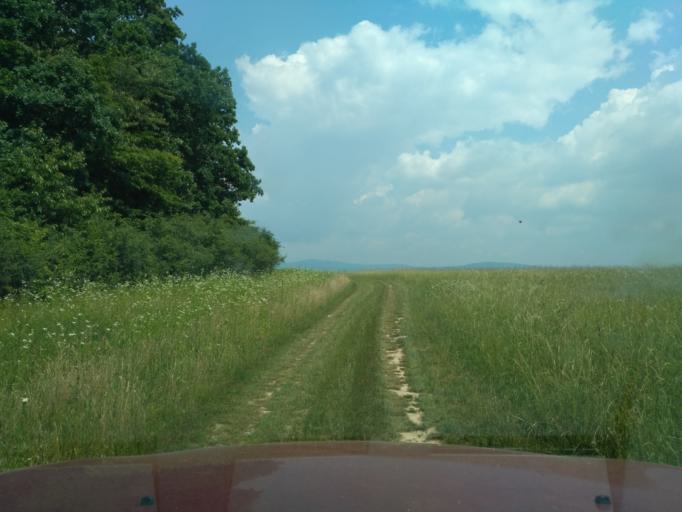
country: SK
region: Kosicky
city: Moldava nad Bodvou
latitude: 48.6245
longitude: 21.0462
